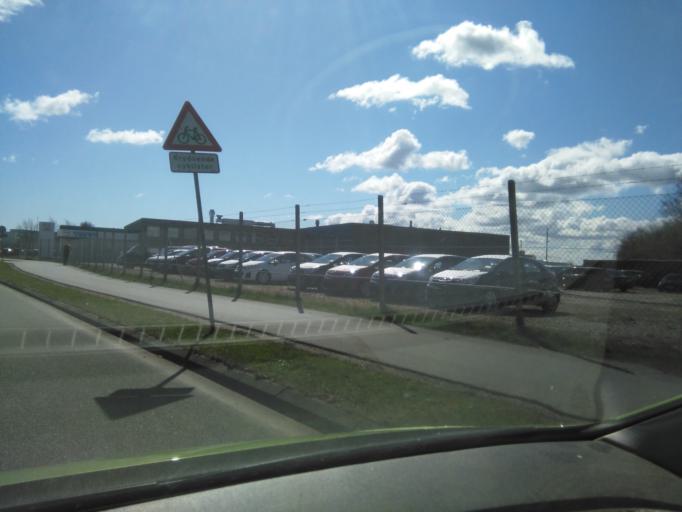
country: DK
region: Central Jutland
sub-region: Arhus Kommune
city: Lystrup
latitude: 56.2058
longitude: 10.2527
